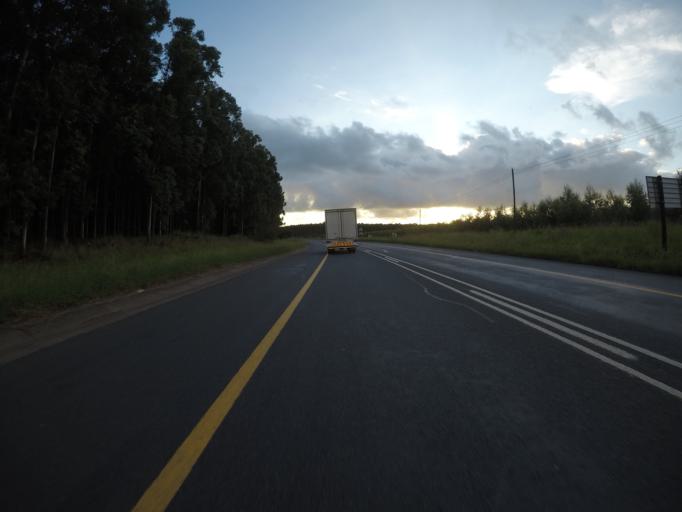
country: ZA
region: KwaZulu-Natal
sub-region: uThungulu District Municipality
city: KwaMbonambi
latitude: -28.5787
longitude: 32.1016
